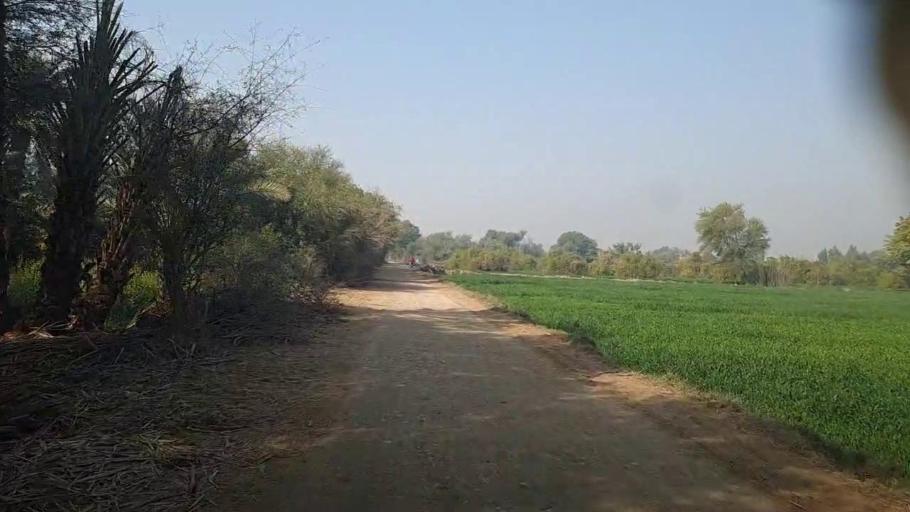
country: PK
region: Sindh
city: Karaundi
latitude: 26.8459
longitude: 68.3771
